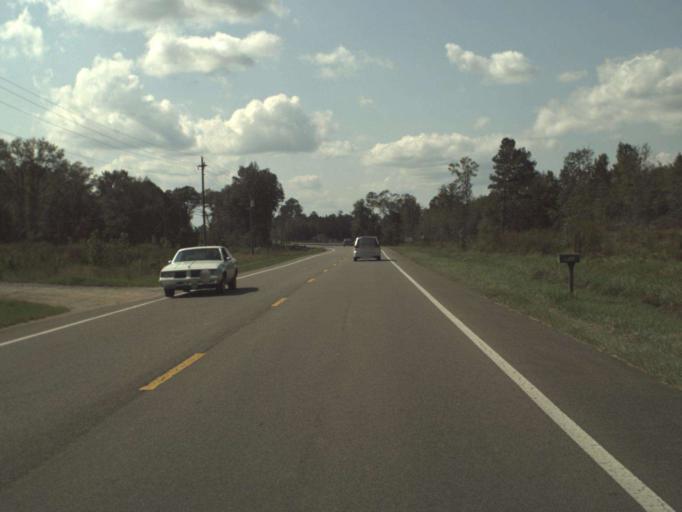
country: US
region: Florida
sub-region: Holmes County
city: Bonifay
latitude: 30.6001
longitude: -85.7592
